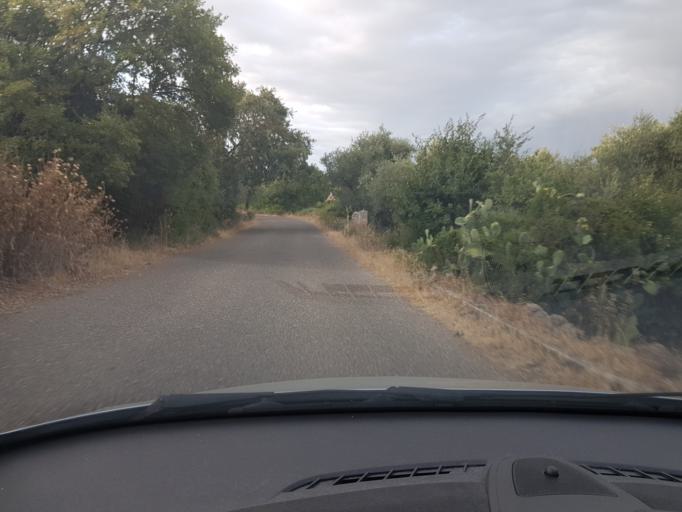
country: IT
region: Sardinia
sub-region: Provincia di Oristano
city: Seneghe
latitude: 40.0903
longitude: 8.6202
